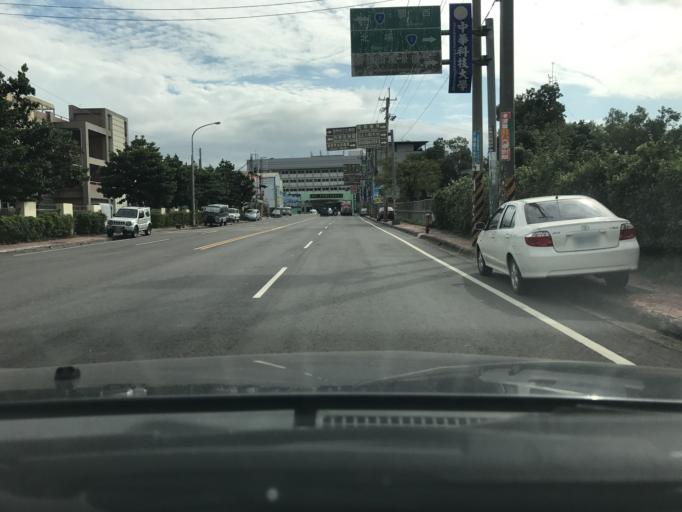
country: TW
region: Taiwan
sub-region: Hsinchu
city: Zhubei
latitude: 24.7249
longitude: 121.0993
